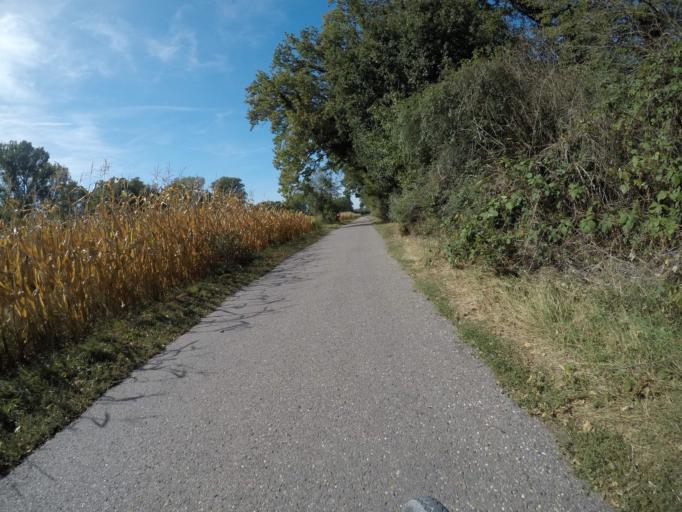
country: DE
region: Baden-Wuerttemberg
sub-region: Karlsruhe Region
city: Ubstadt-Weiher
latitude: 49.1530
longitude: 8.6504
